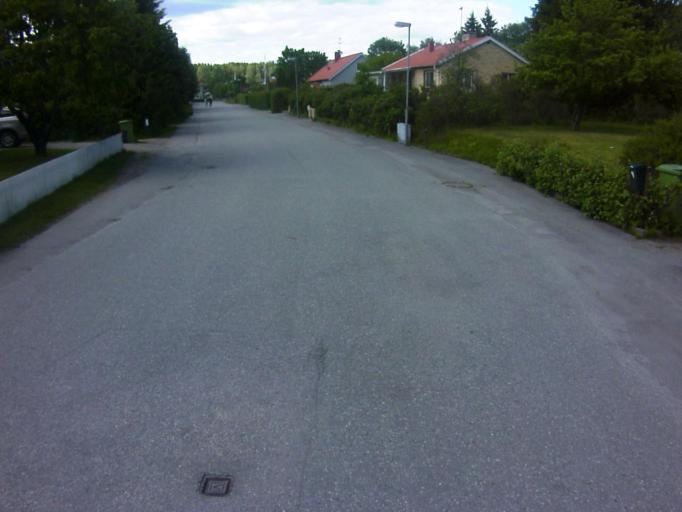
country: SE
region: Soedermanland
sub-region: Eskilstuna Kommun
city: Skogstorp
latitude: 59.3249
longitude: 16.4900
